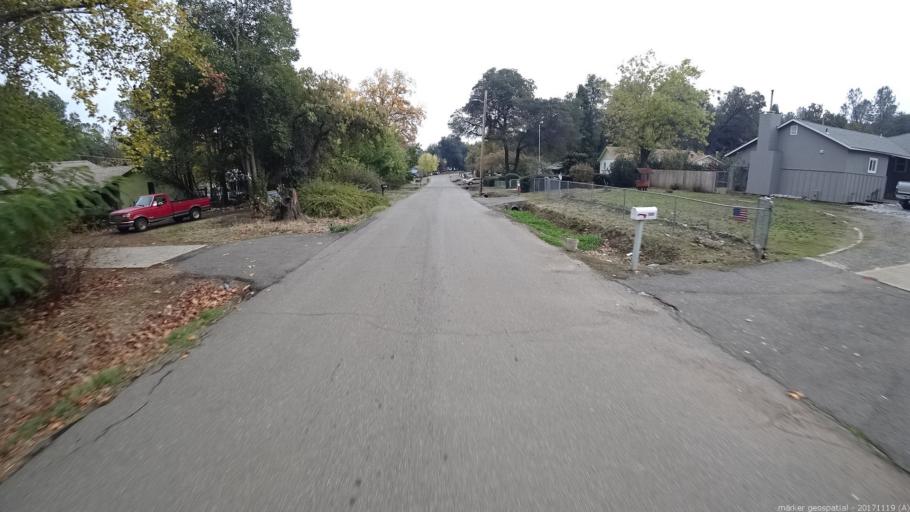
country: US
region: California
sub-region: Shasta County
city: Anderson
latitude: 40.4895
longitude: -122.3719
